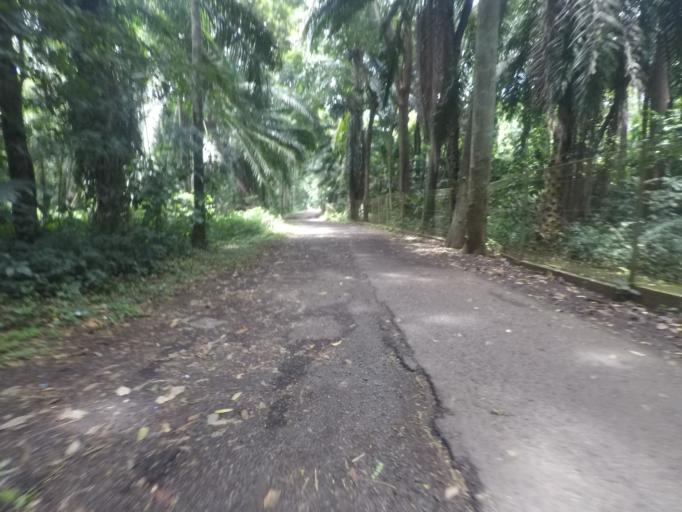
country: ID
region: West Java
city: Ciampea
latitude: -6.5536
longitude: 106.7530
